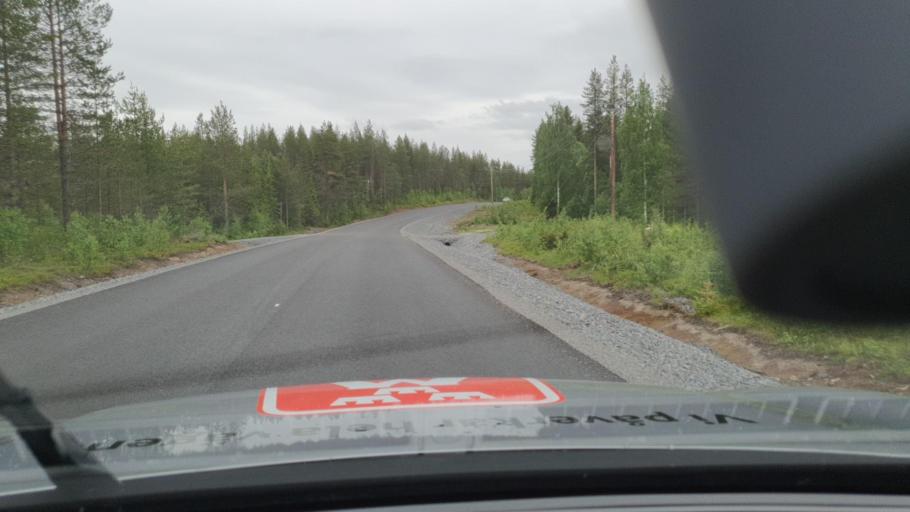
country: SE
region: Norrbotten
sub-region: Overkalix Kommun
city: OEverkalix
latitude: 66.6708
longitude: 23.2215
